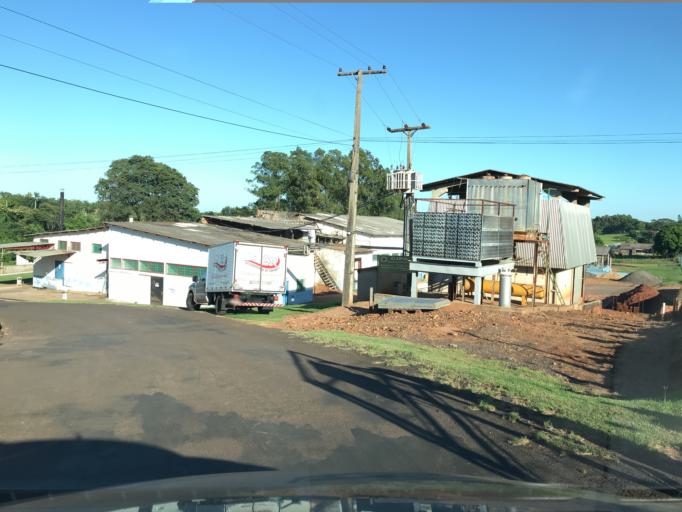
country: BR
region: Parana
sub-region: Ipora
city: Ipora
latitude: -23.9935
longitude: -53.7085
